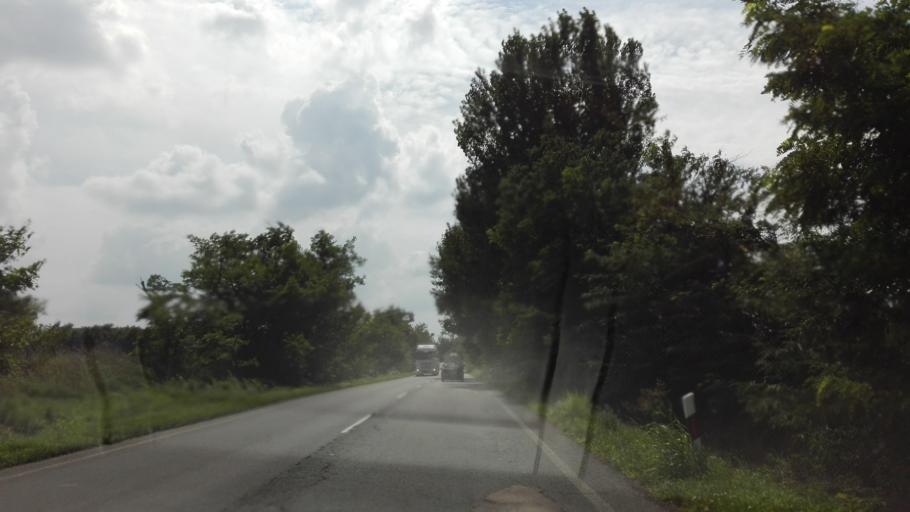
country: HU
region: Fejer
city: Alap
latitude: 46.7801
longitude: 18.6713
